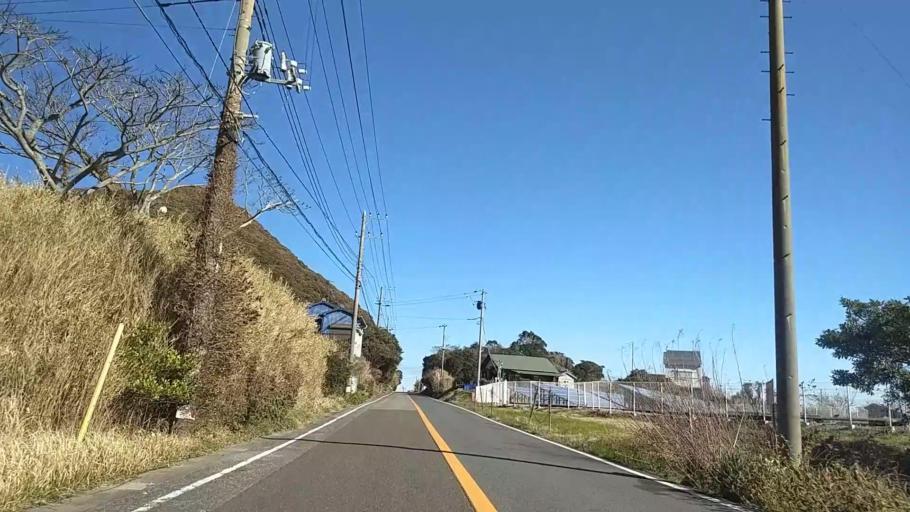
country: JP
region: Chiba
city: Tateyama
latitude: 34.9158
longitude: 139.9328
